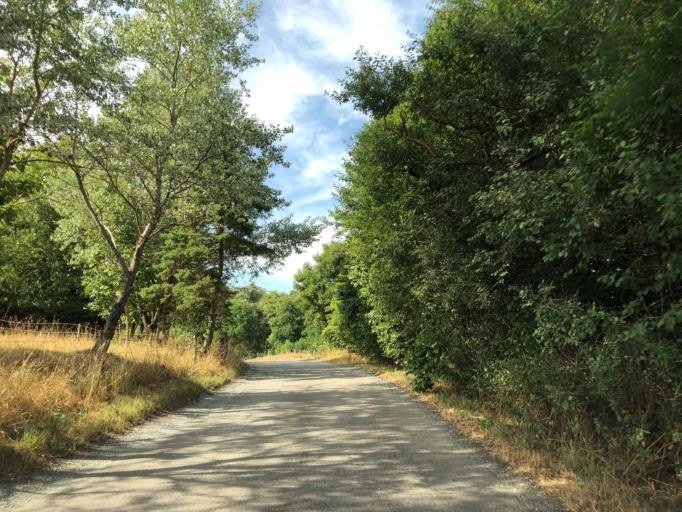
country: DK
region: South Denmark
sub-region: Vejle Kommune
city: Egtved
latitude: 55.6526
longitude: 9.3054
